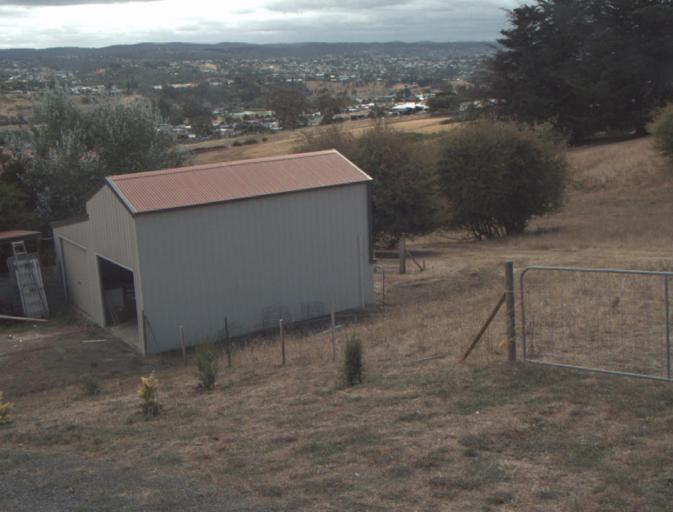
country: AU
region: Tasmania
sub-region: Launceston
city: Newstead
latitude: -41.4537
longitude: 147.2070
